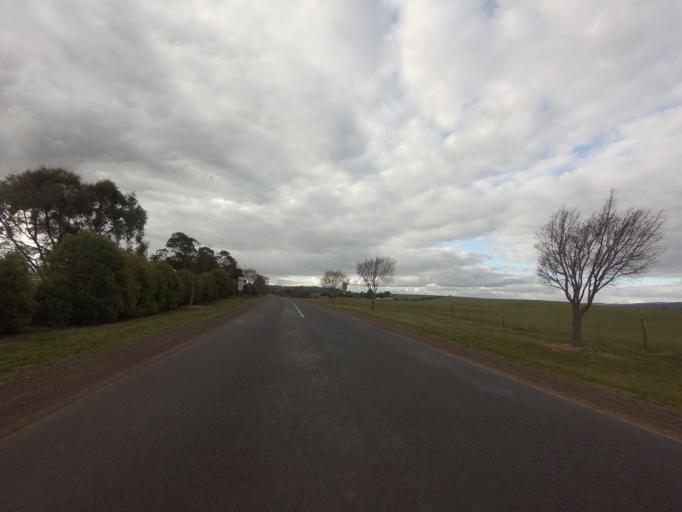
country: AU
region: Tasmania
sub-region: Northern Midlands
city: Evandale
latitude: -42.0251
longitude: 147.4933
